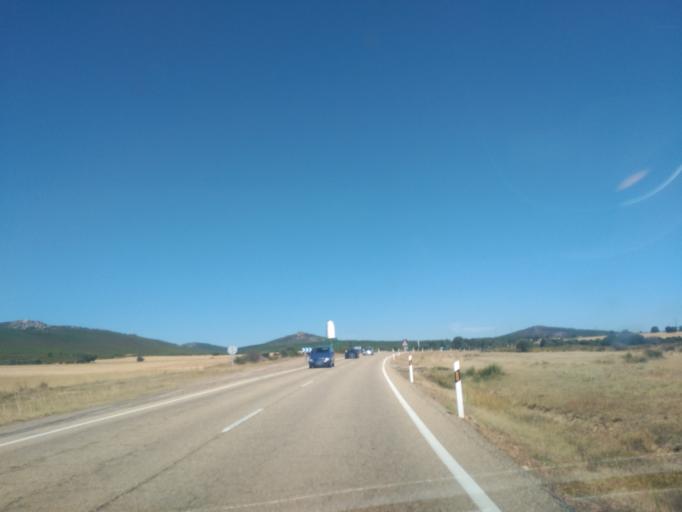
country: ES
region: Castille and Leon
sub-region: Provincia de Zamora
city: Tabara
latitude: 41.8536
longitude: -5.9909
